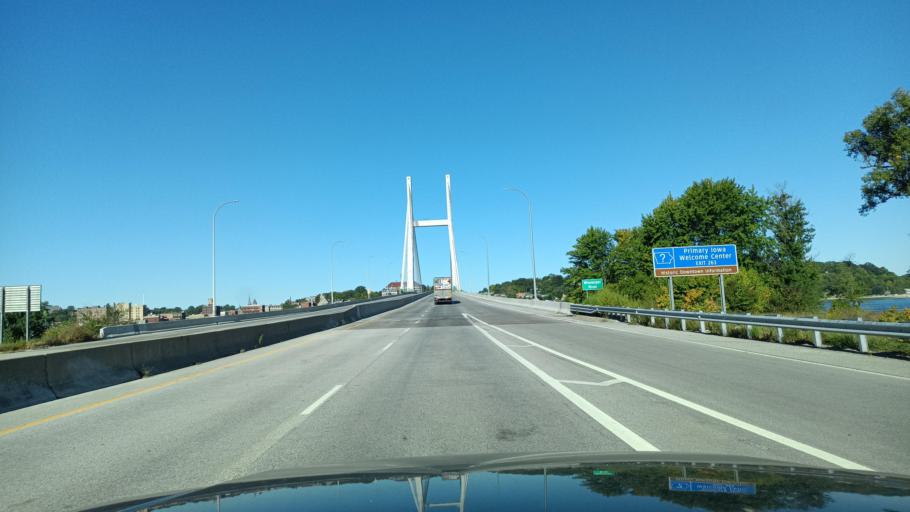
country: US
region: Iowa
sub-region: Des Moines County
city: Burlington
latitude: 40.8107
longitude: -91.0905
